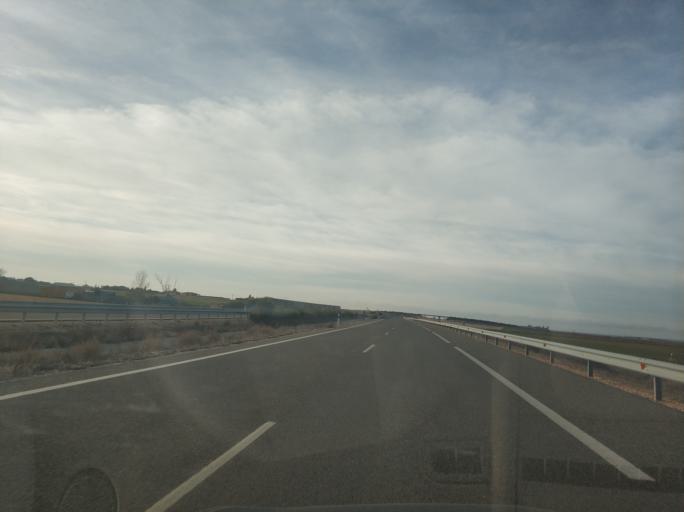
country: ES
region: Castille and Leon
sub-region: Provincia de Salamanca
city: Castellanos de Villiquera
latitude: 41.0535
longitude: -5.6731
